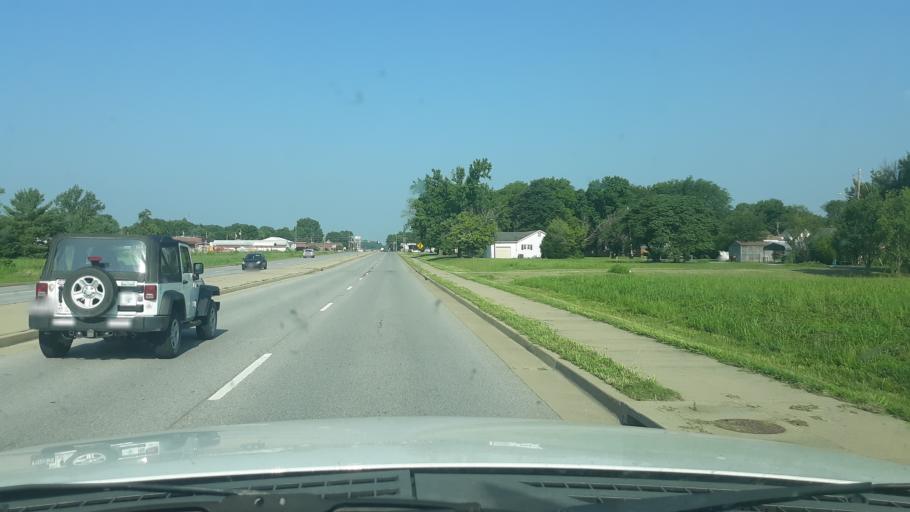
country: US
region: Illinois
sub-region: Saline County
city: Harrisburg
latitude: 37.7434
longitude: -88.5348
